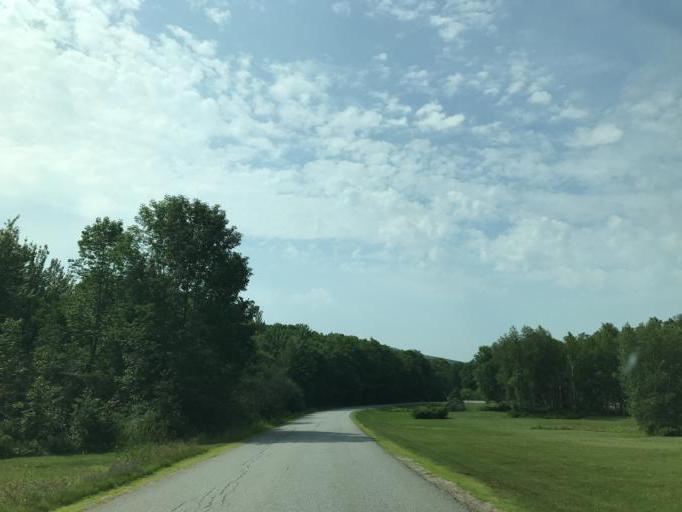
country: US
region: Maine
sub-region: Knox County
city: Hope
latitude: 44.2122
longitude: -69.1700
